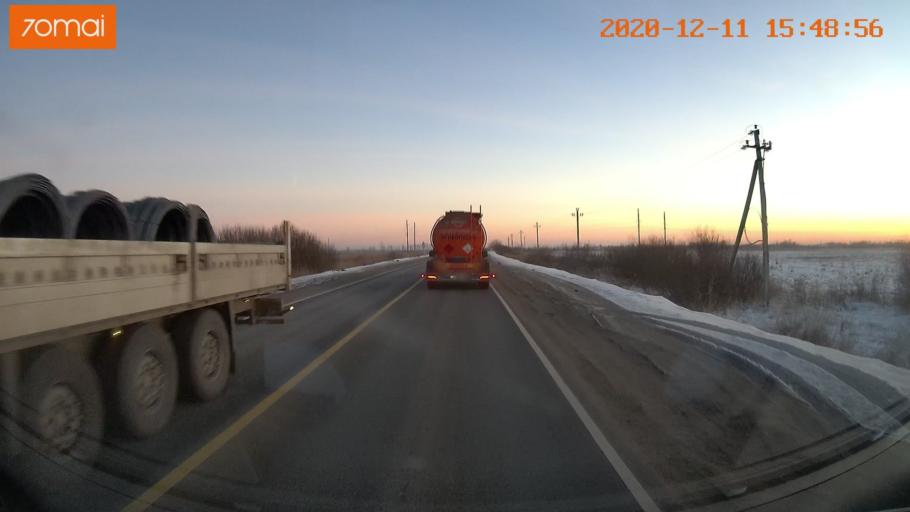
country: RU
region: Ivanovo
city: Novo-Talitsy
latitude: 56.9910
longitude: 40.8708
